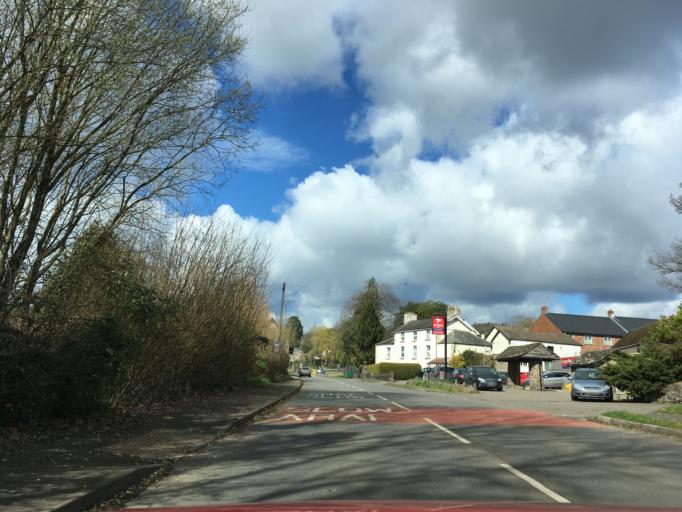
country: GB
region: Wales
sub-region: Monmouthshire
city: Chepstow
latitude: 51.6631
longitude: -2.6964
